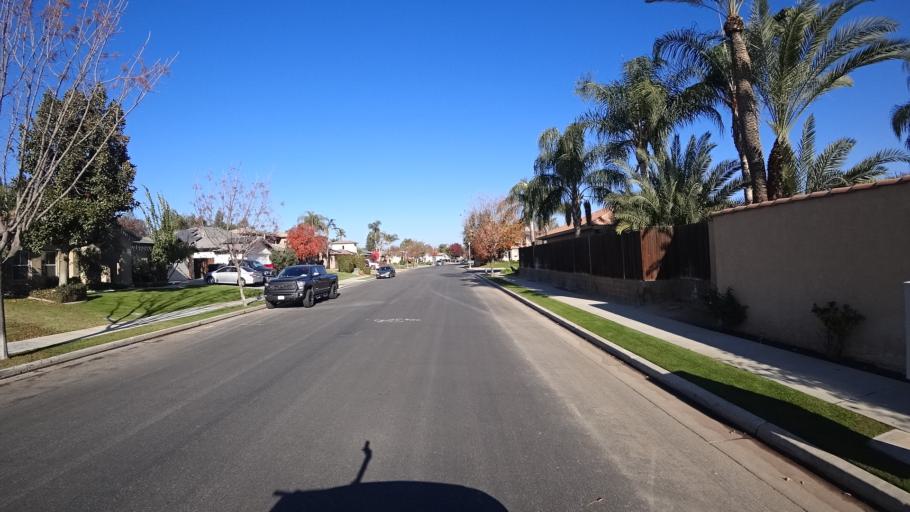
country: US
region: California
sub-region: Kern County
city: Rosedale
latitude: 35.3284
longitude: -119.1304
